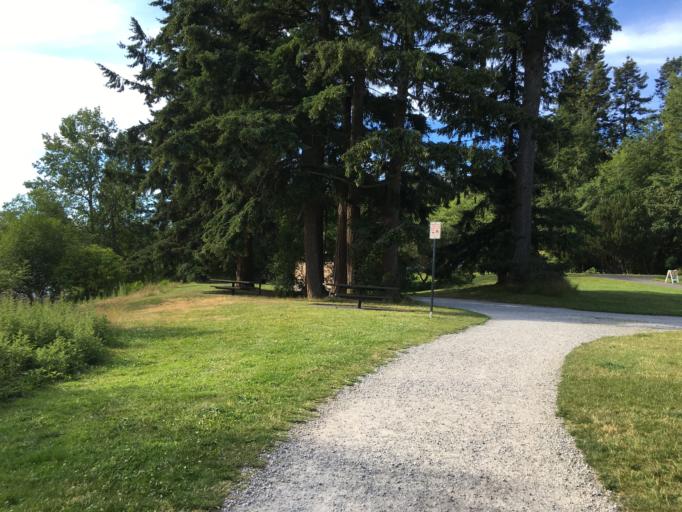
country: US
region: Washington
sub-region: Whatcom County
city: Geneva
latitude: 48.7000
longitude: -122.4461
